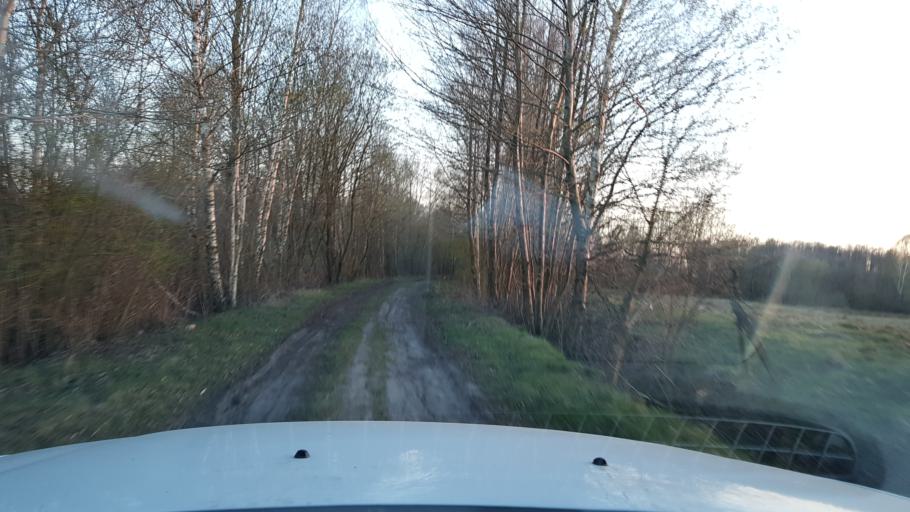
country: PL
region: West Pomeranian Voivodeship
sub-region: Powiat bialogardzki
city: Bialogard
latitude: 53.9780
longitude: 15.9576
